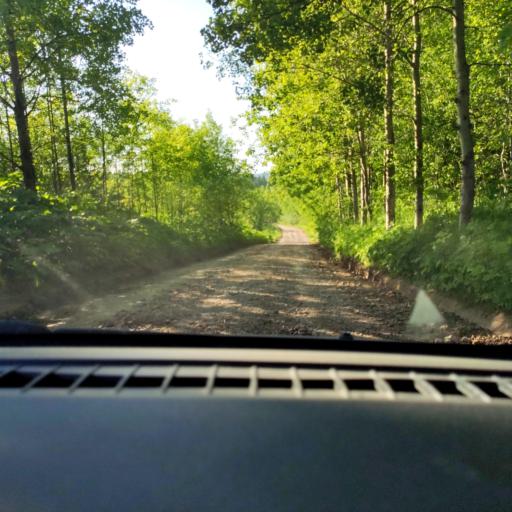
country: RU
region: Perm
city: Overyata
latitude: 58.1254
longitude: 55.8773
